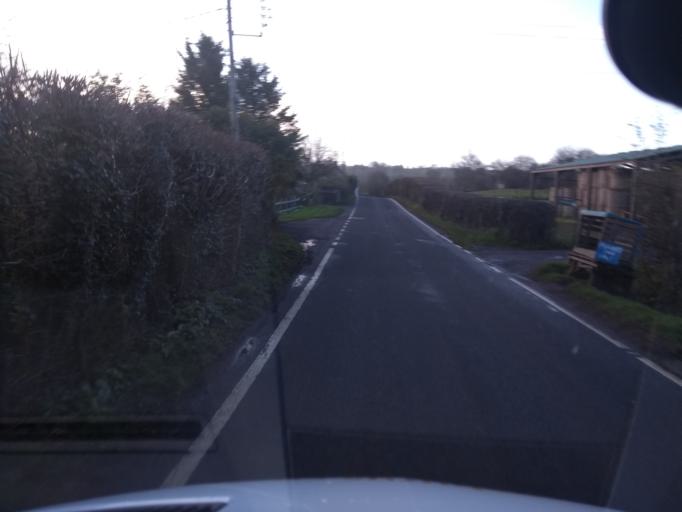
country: GB
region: England
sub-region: Somerset
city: Wedmore
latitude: 51.2206
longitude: -2.7902
